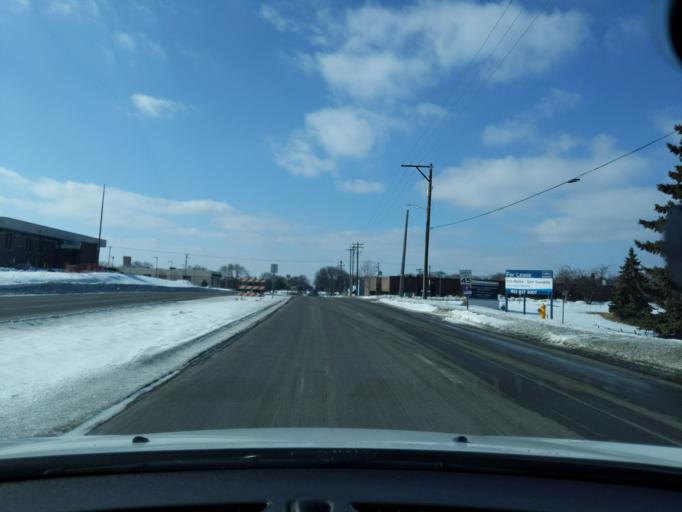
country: US
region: Minnesota
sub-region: Hennepin County
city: Saint Anthony
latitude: 45.0207
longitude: -93.2057
